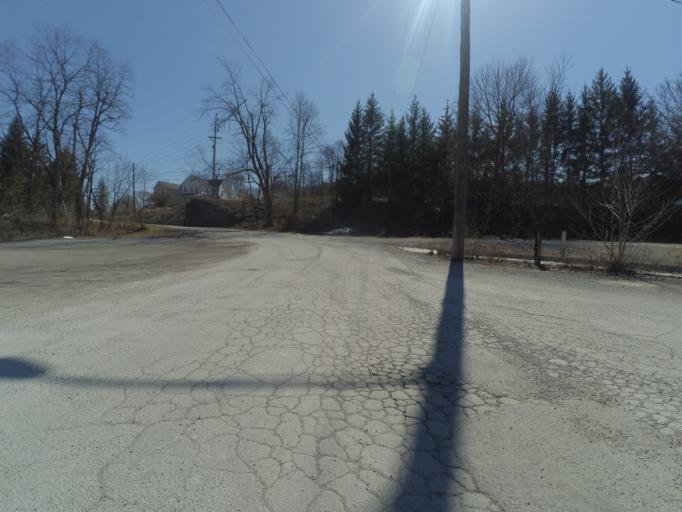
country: US
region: Pennsylvania
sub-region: Centre County
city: Bellefonte
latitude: 40.9152
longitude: -77.7867
